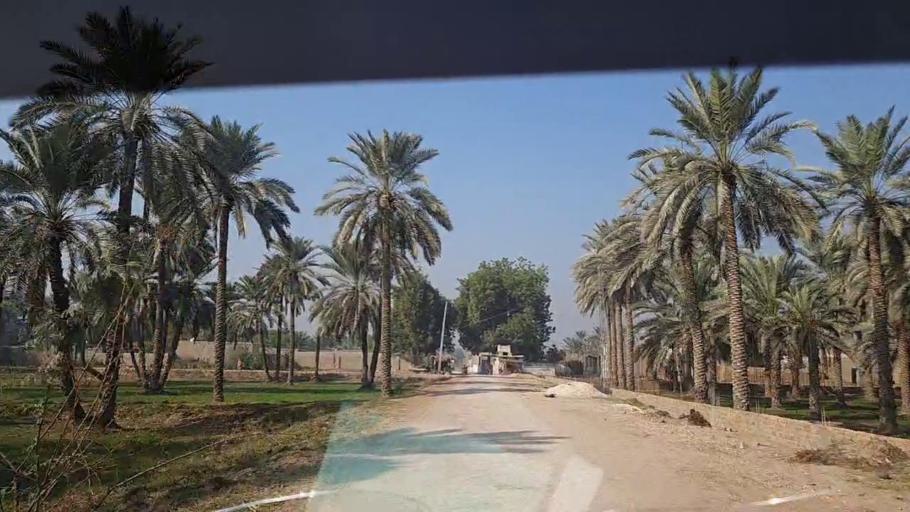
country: PK
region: Sindh
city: Khairpur
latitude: 27.4917
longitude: 68.7554
